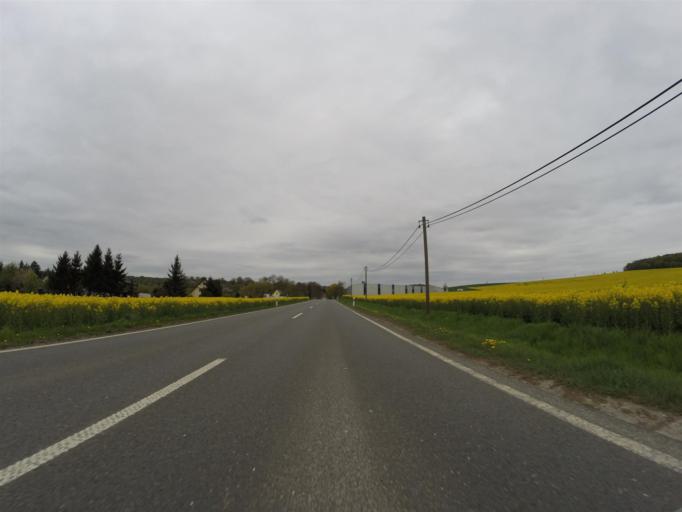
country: DE
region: Thuringia
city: Camburg
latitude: 51.0665
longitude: 11.7252
